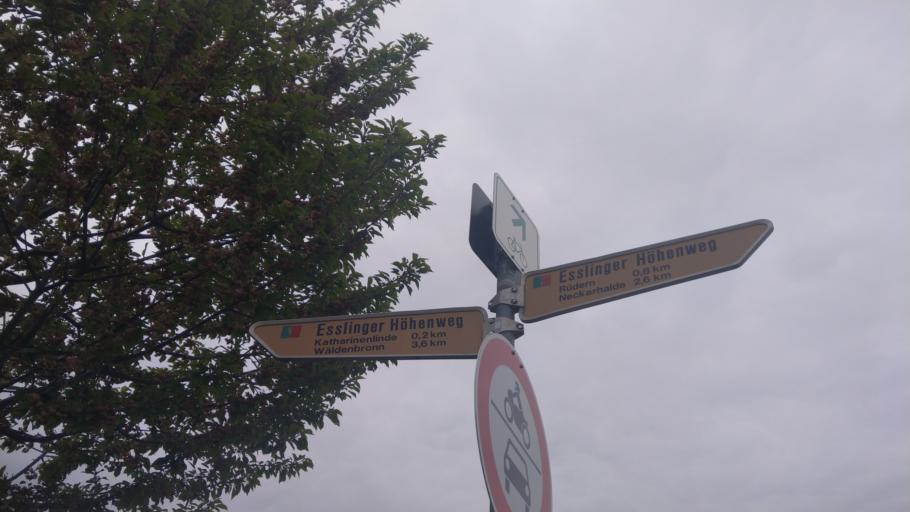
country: DE
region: Baden-Wuerttemberg
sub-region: Regierungsbezirk Stuttgart
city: Esslingen
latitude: 48.7689
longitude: 9.2918
